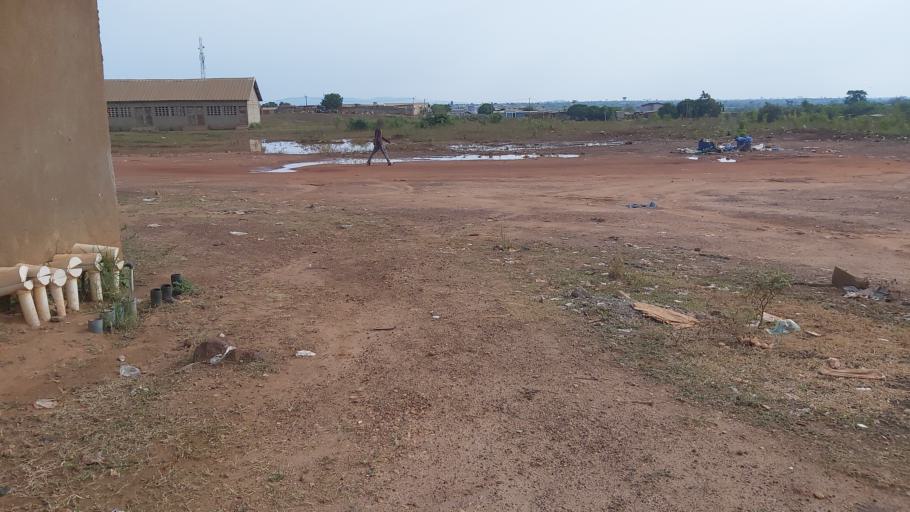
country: CI
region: Lacs
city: Yamoussoukro
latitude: 6.7856
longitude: -5.2787
